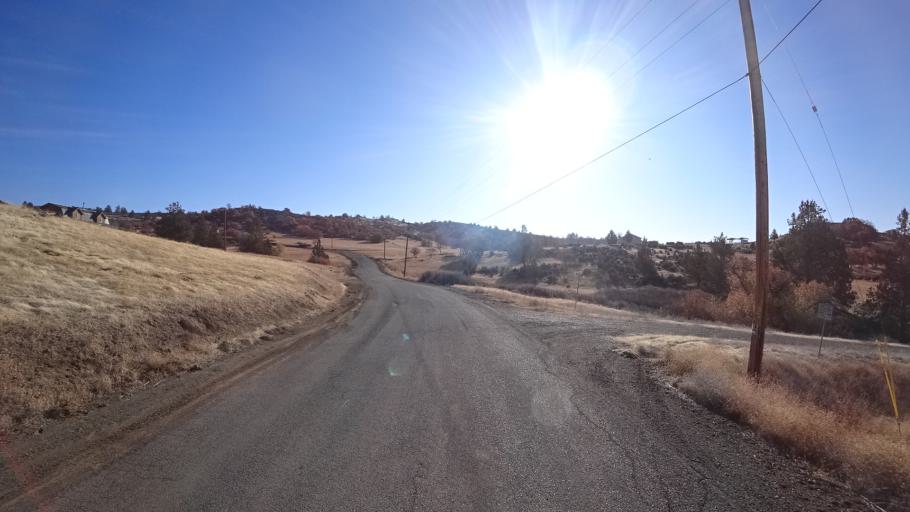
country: US
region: California
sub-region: Siskiyou County
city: Montague
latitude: 41.8760
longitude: -122.4666
